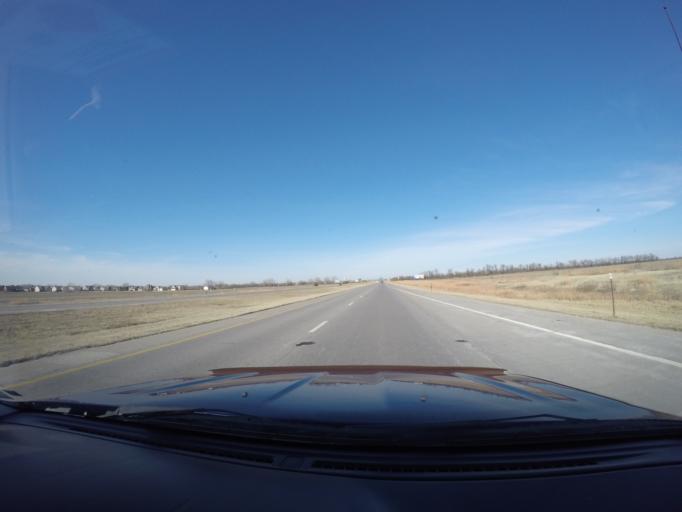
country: US
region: Kansas
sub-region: Harvey County
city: Newton
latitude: 38.0032
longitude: -97.3279
